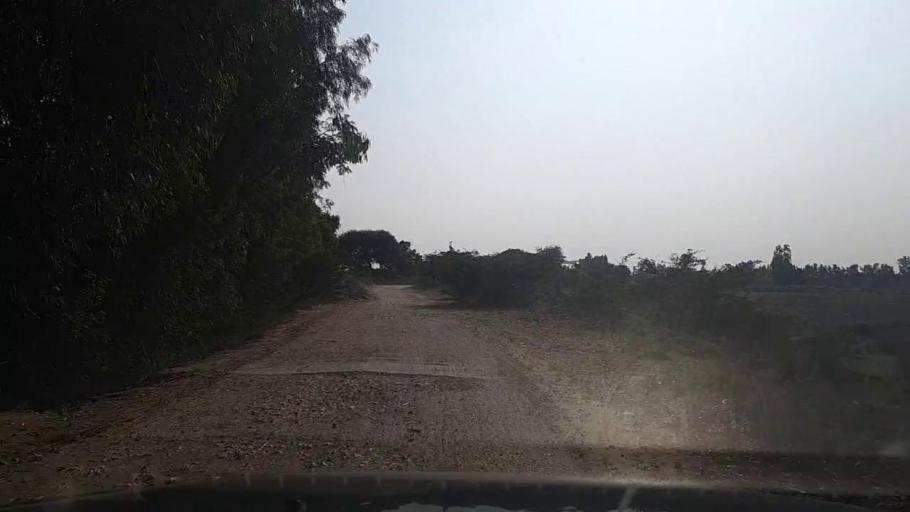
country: PK
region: Sindh
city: Mirpur Sakro
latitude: 24.6276
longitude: 67.7560
